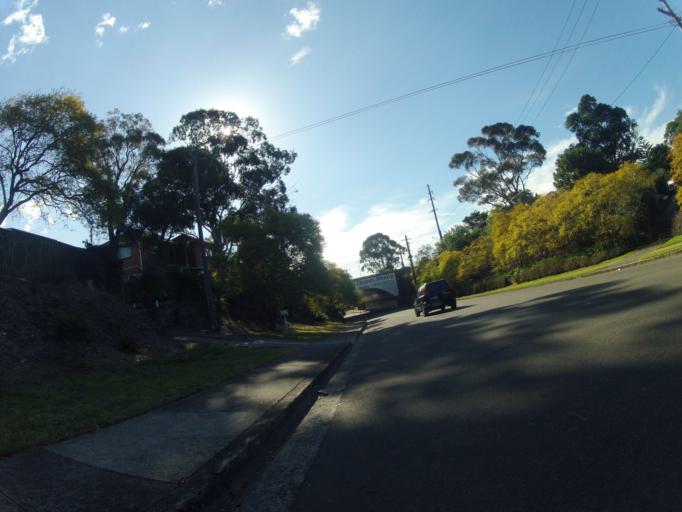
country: AU
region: New South Wales
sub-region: Hurstville
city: Penshurst
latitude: -33.9707
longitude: 151.0821
